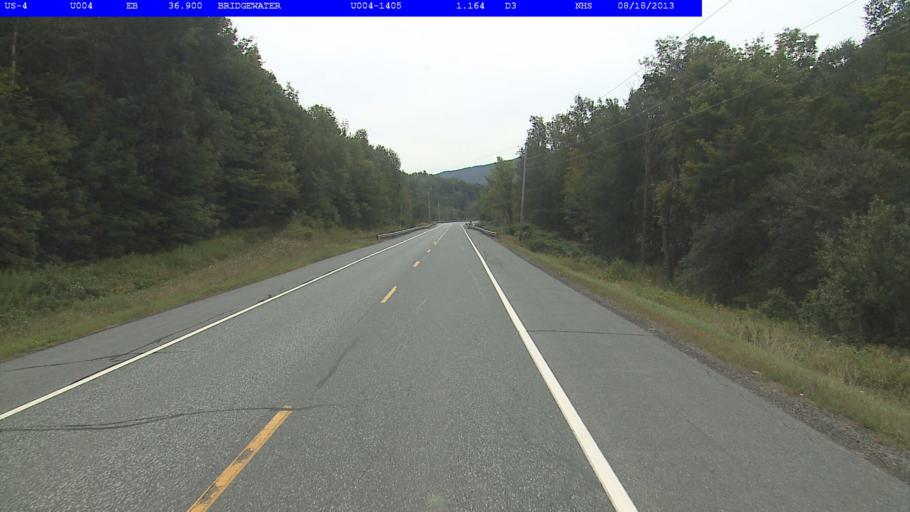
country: US
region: Vermont
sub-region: Windsor County
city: Woodstock
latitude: 43.6031
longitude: -72.7285
